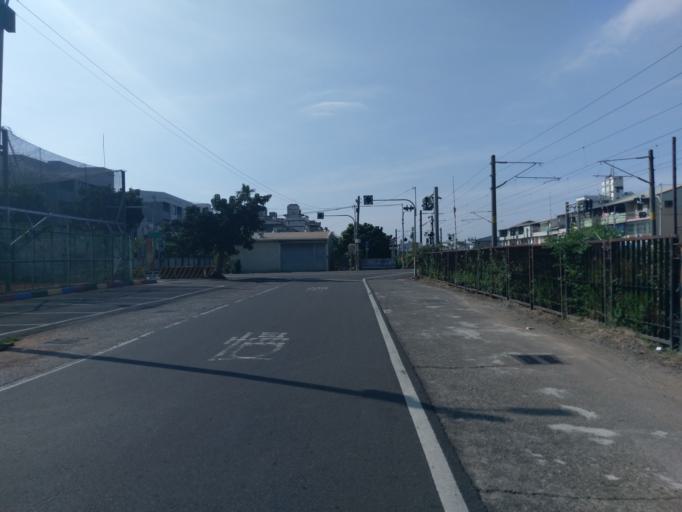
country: TW
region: Taiwan
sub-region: Yunlin
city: Douliu
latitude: 23.7143
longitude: 120.5517
